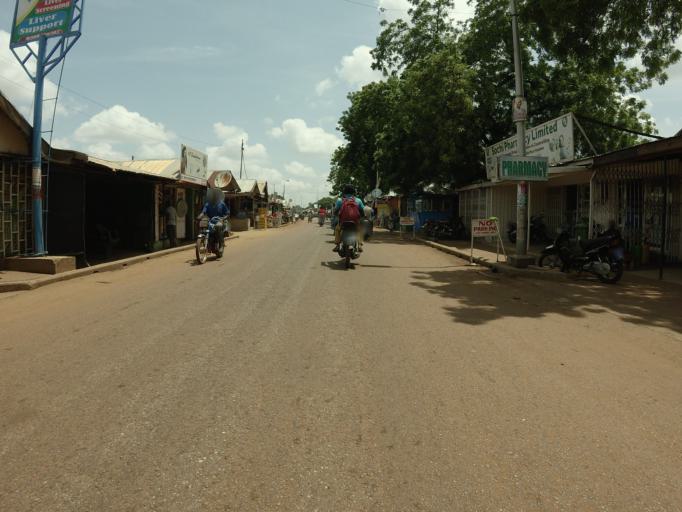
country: GH
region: Northern
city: Tamale
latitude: 9.4015
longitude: -0.8435
